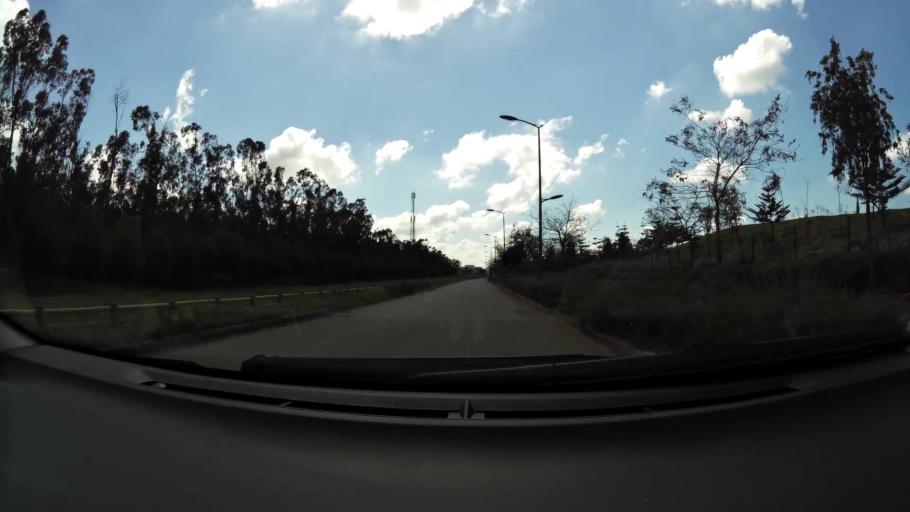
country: MA
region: Grand Casablanca
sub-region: Nouaceur
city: Bouskoura
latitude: 33.4752
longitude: -7.5965
